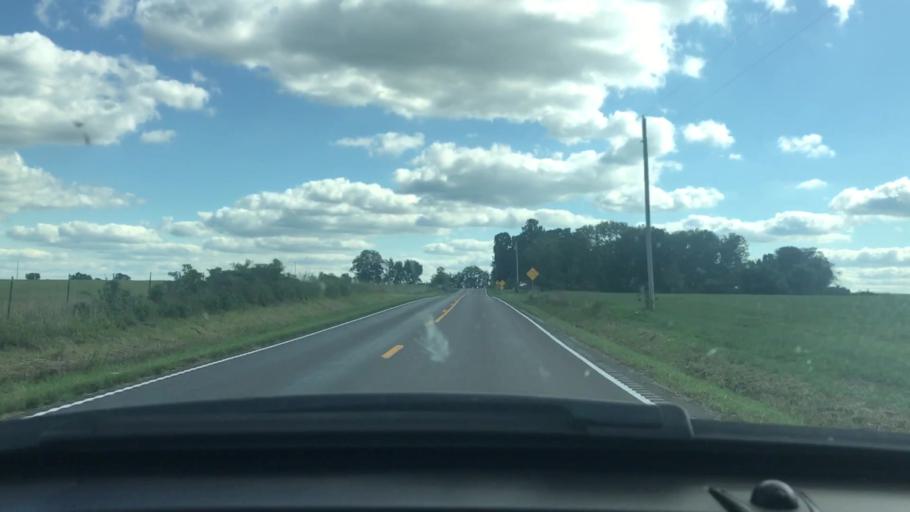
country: US
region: Missouri
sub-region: Wright County
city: Mountain Grove
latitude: 37.1687
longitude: -92.2672
